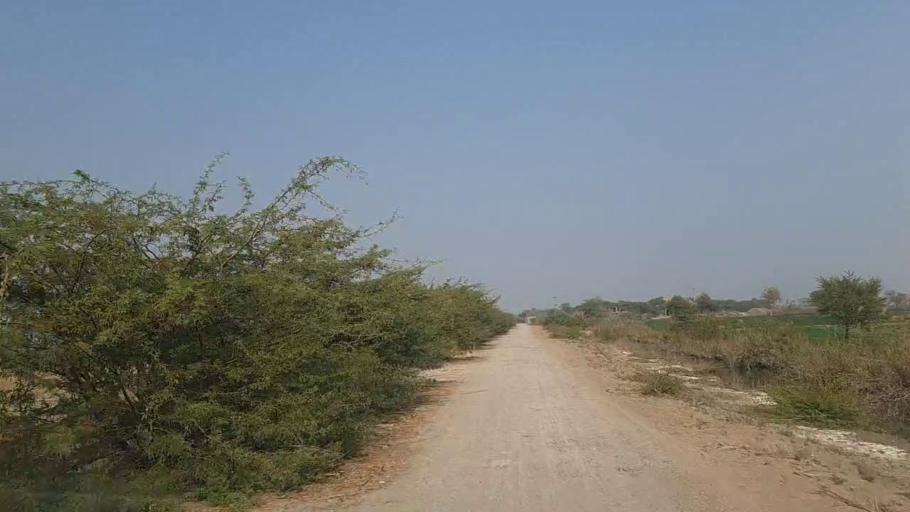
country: PK
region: Sindh
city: Daur
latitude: 26.4363
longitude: 68.4426
